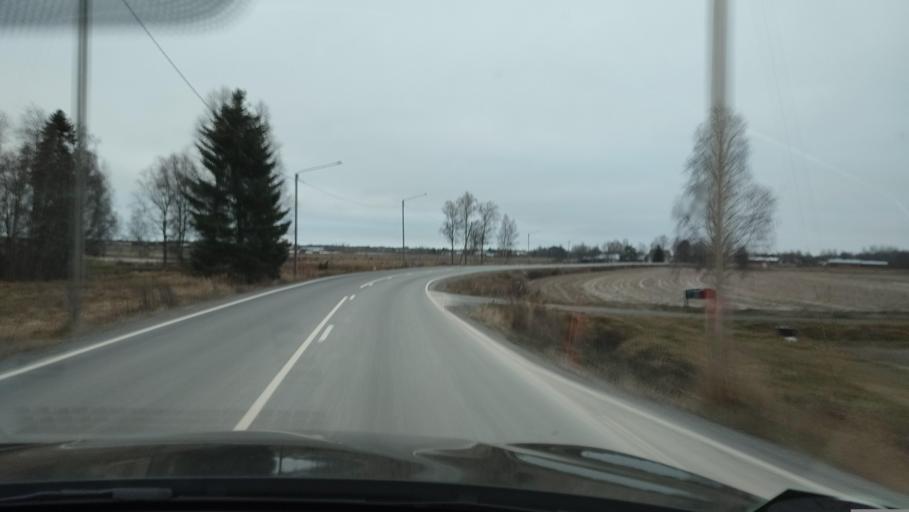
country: FI
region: Southern Ostrobothnia
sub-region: Suupohja
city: Karijoki
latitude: 62.2706
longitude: 21.5610
